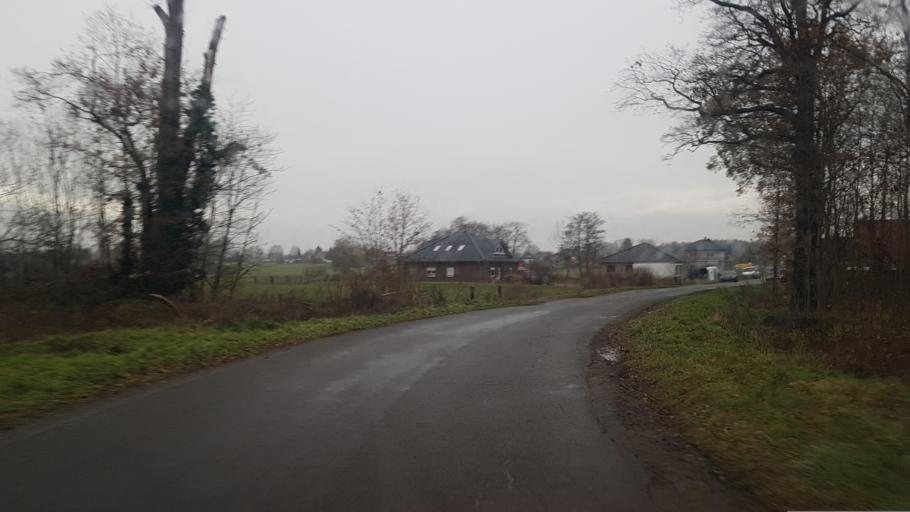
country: DE
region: Brandenburg
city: Drebkau
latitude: 51.6875
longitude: 14.2823
